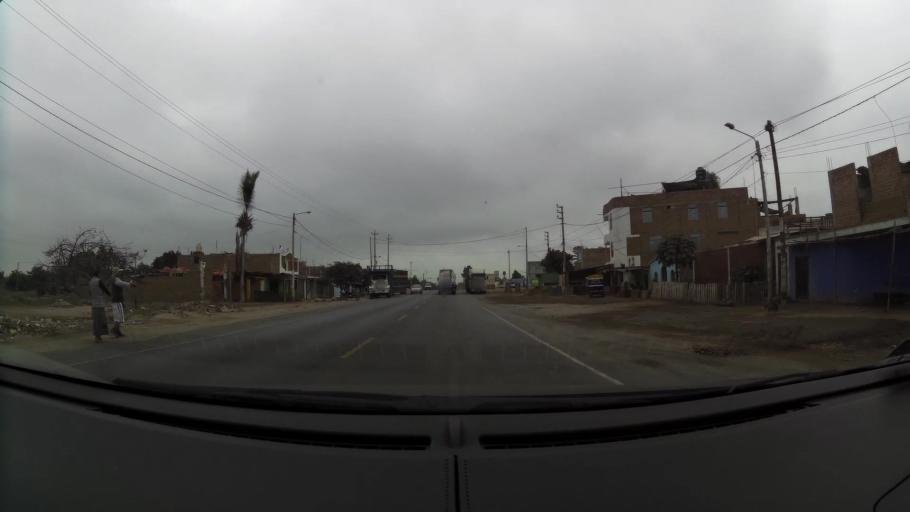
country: PE
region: La Libertad
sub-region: Viru
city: Viru
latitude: -8.4334
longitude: -78.7702
